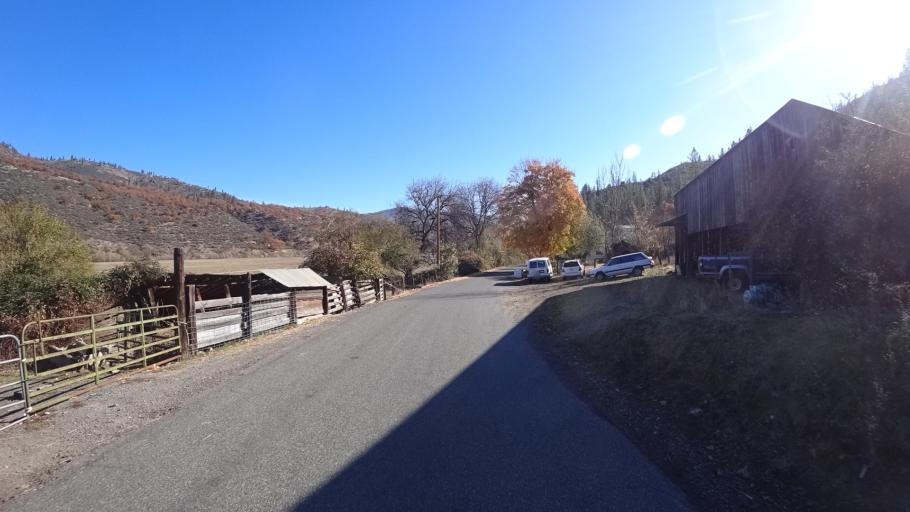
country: US
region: California
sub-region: Siskiyou County
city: Yreka
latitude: 41.8350
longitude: -122.8637
